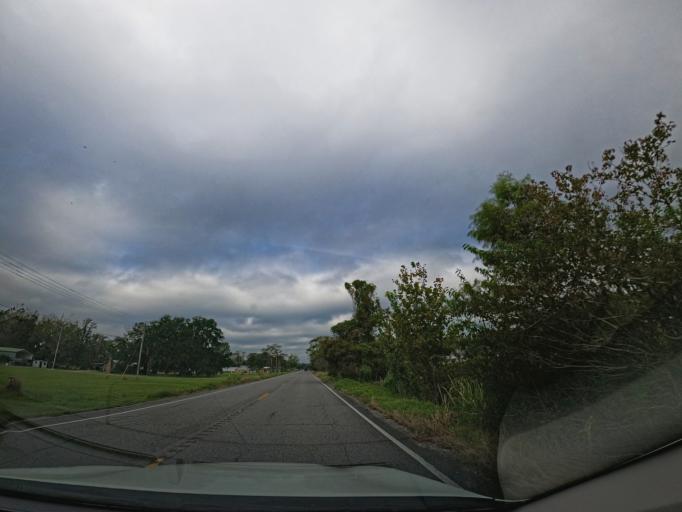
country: US
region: Louisiana
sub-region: Saint Mary Parish
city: Amelia
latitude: 29.6381
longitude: -90.9533
